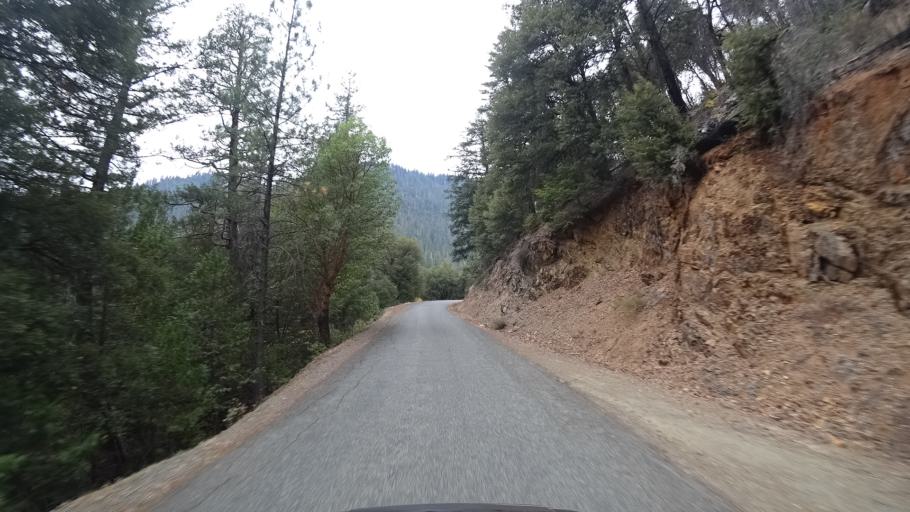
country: US
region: California
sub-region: Siskiyou County
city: Happy Camp
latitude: 41.7647
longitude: -123.3641
